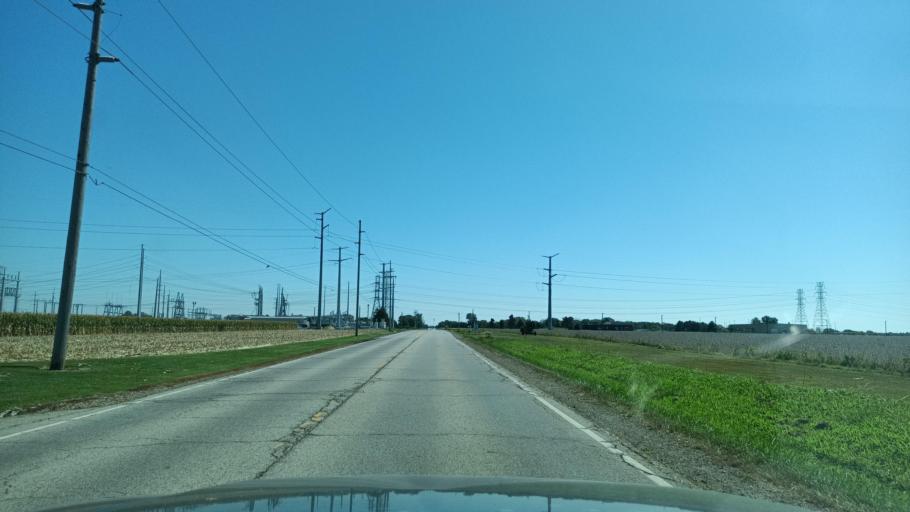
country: US
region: Illinois
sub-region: Peoria County
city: Dunlap
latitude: 40.7823
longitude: -89.7037
